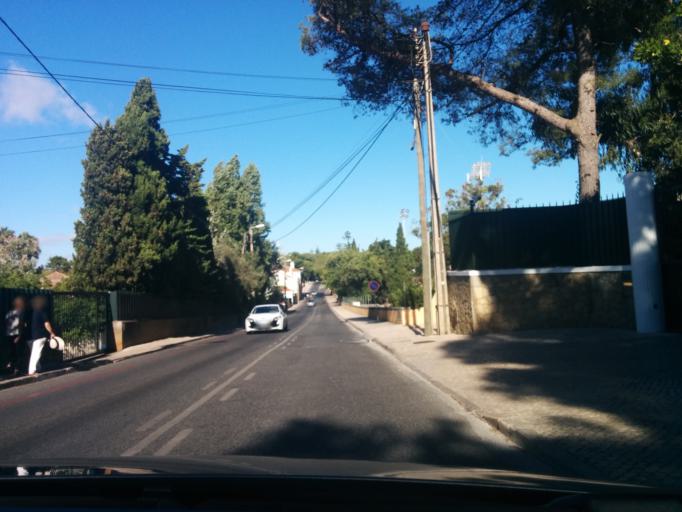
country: PT
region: Lisbon
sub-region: Cascais
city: Cascais
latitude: 38.6942
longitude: -9.4268
